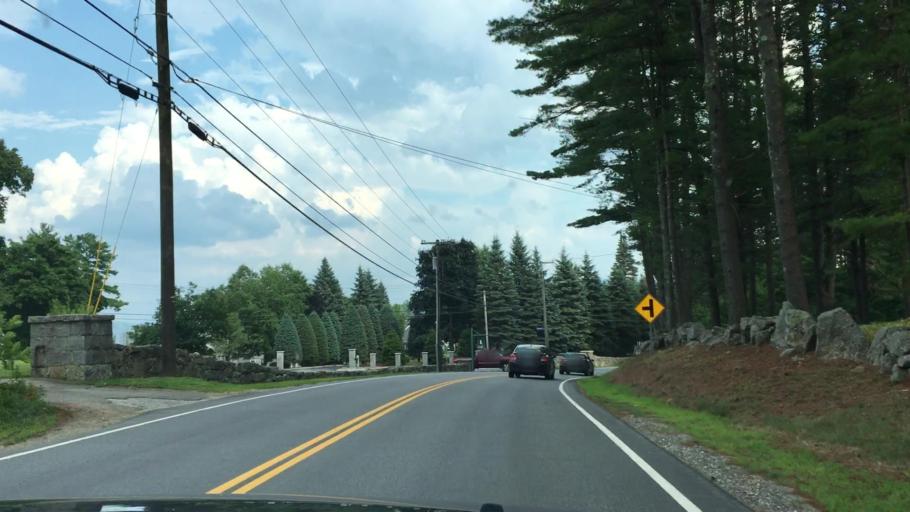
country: US
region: New Hampshire
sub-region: Belknap County
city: Gilford
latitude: 43.6000
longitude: -71.4334
